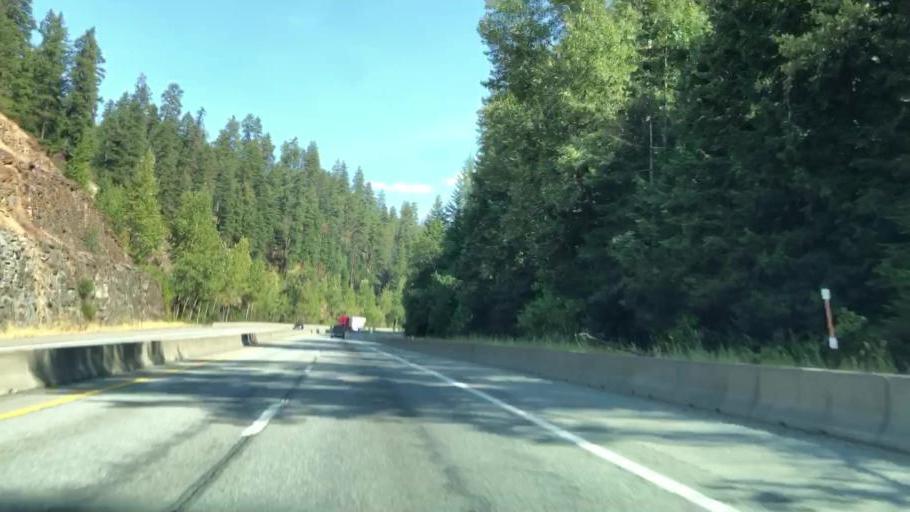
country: US
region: Idaho
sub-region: Kootenai County
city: Coeur d'Alene
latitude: 47.6243
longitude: -116.5655
